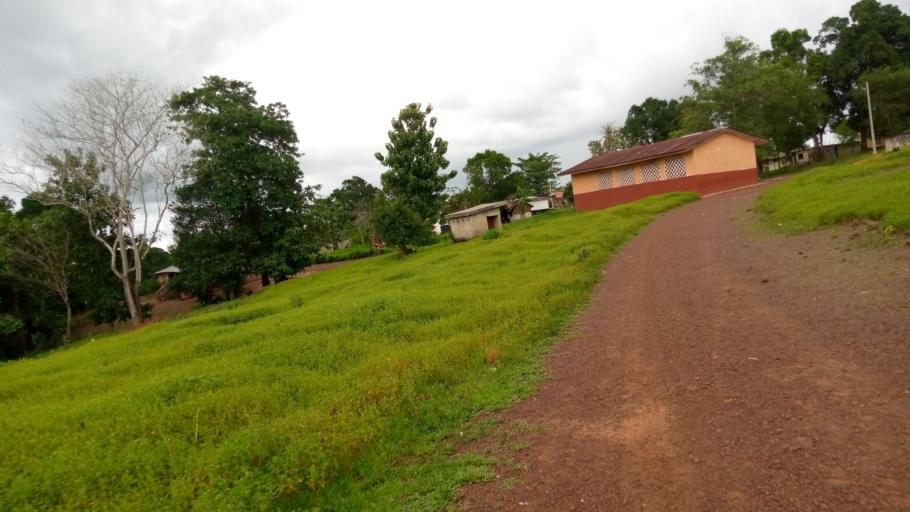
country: SL
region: Southern Province
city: Moyamba
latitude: 8.1644
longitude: -12.4418
